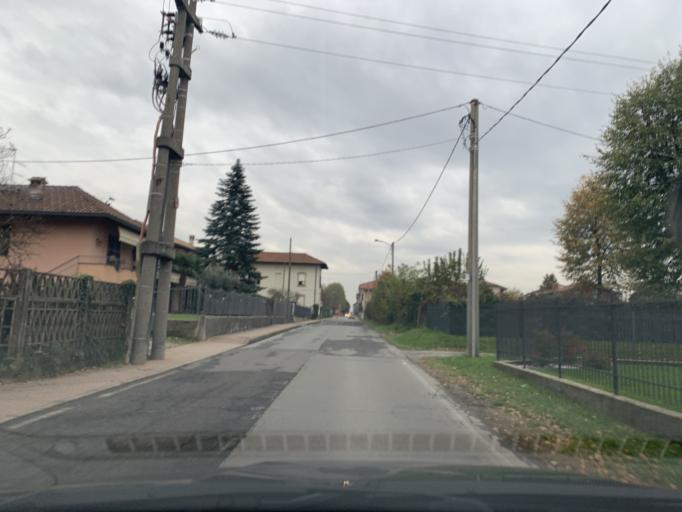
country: IT
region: Lombardy
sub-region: Provincia di Como
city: Bregnano
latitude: 45.7023
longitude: 9.0575
